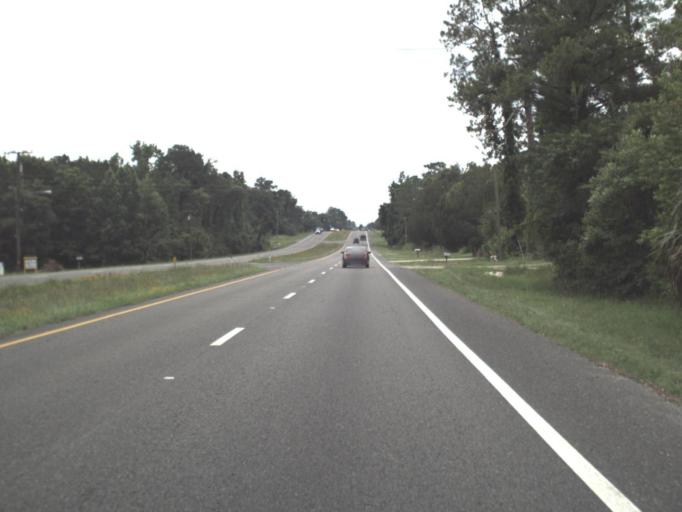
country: US
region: Florida
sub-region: Nassau County
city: Hilliard
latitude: 30.7053
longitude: -81.9278
